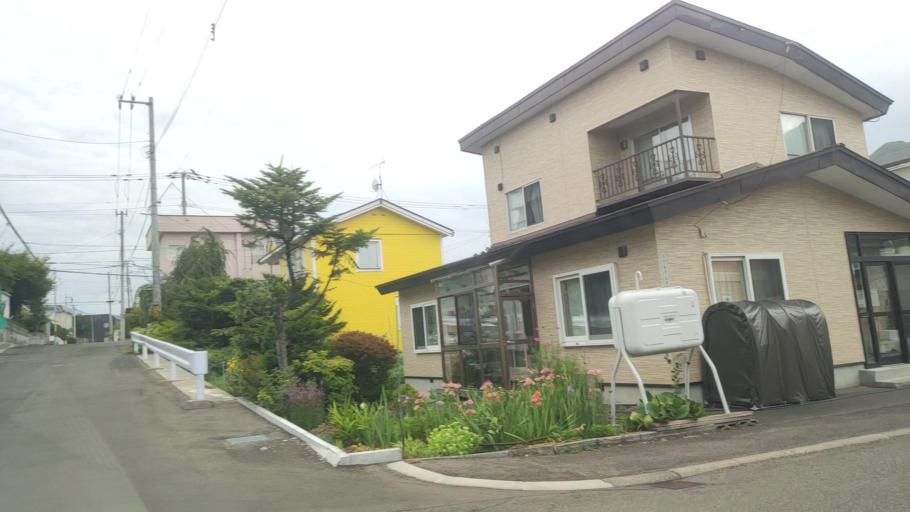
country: JP
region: Hokkaido
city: Sapporo
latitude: 42.9630
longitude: 141.3175
